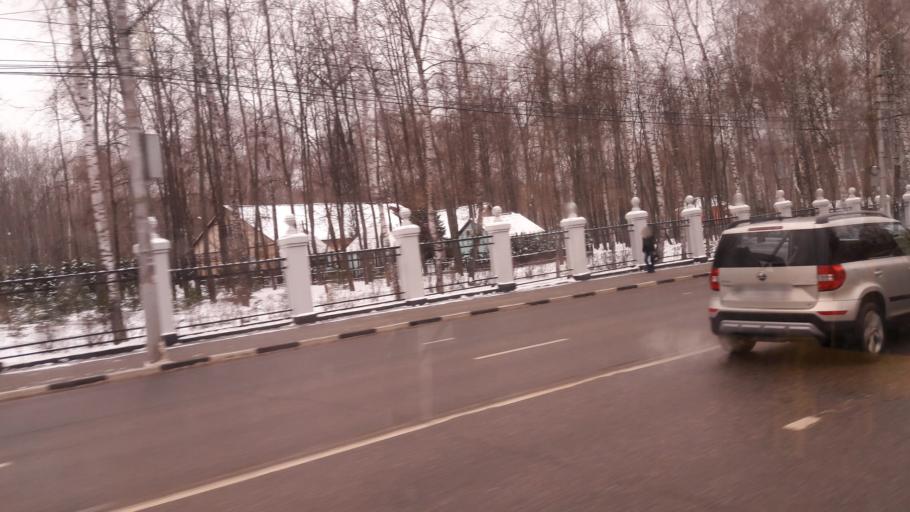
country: RU
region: Tula
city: Gorelki
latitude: 54.2289
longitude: 37.6279
